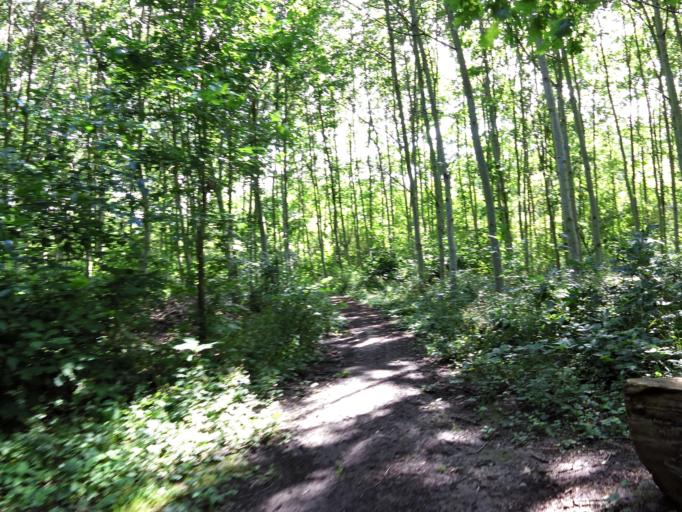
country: DE
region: Saxony
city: Markkleeberg
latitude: 51.3027
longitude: 12.4107
